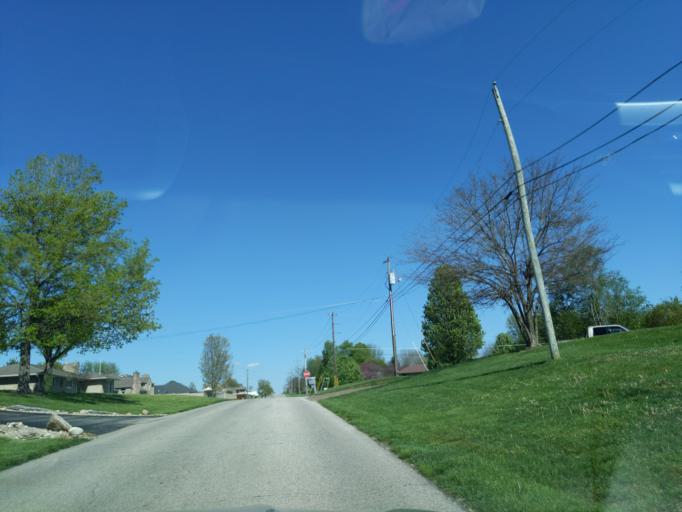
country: US
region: Indiana
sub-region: Decatur County
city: Greensburg
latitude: 39.3289
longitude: -85.5093
